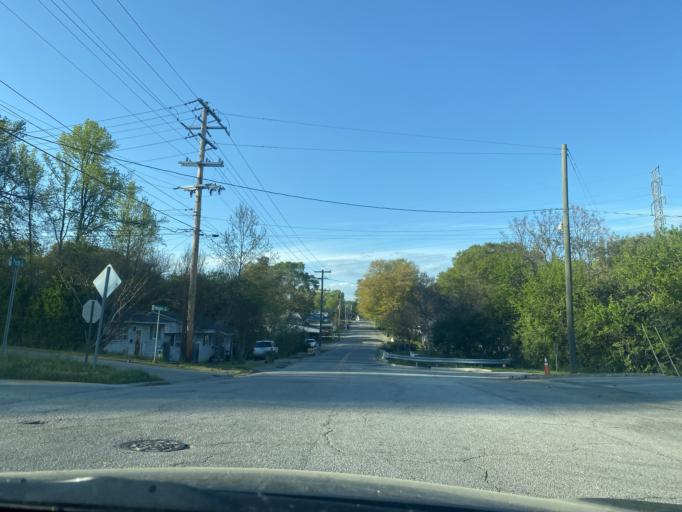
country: US
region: South Carolina
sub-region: Cherokee County
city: East Gaffney
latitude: 35.0715
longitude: -81.6355
